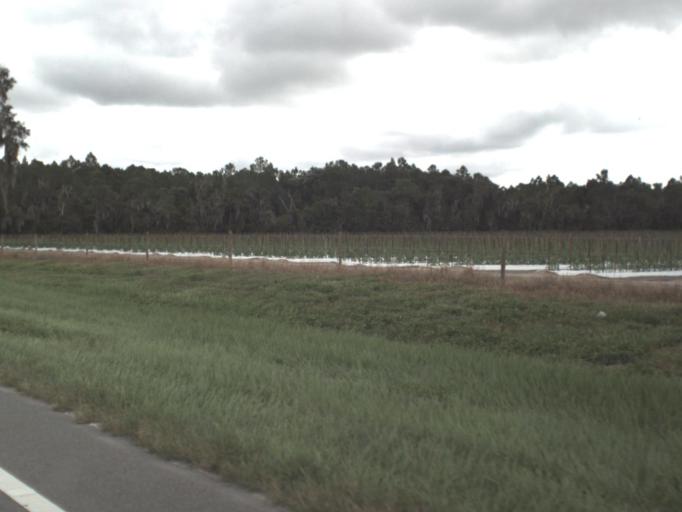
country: US
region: Florida
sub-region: Hillsborough County
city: Wimauma
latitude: 27.5900
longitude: -82.1314
